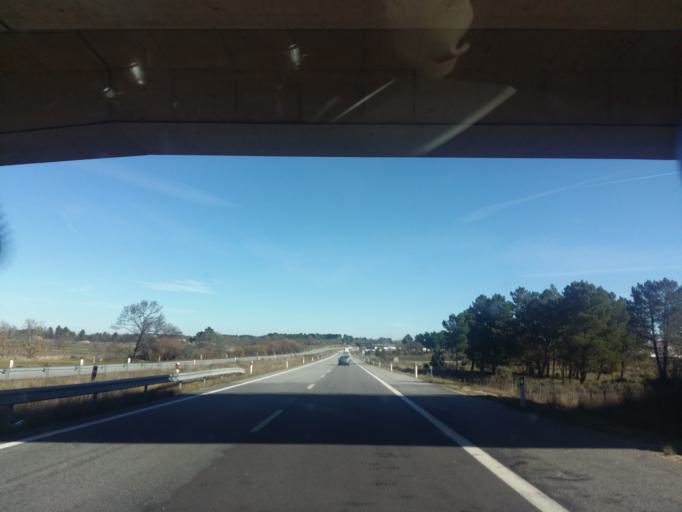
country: PT
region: Guarda
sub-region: Guarda
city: Sequeira
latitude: 40.6011
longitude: -7.1117
